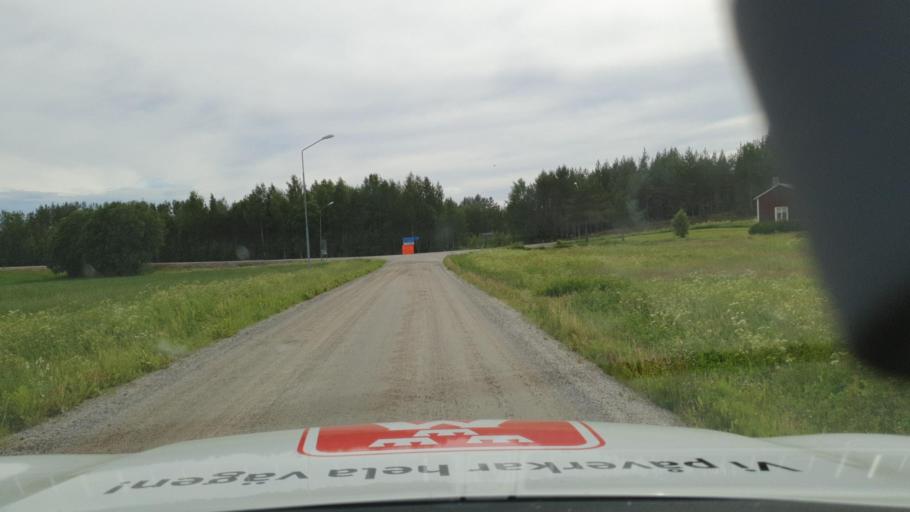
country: SE
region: Vaesterbotten
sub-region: Robertsfors Kommun
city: Robertsfors
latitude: 64.4131
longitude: 21.0016
